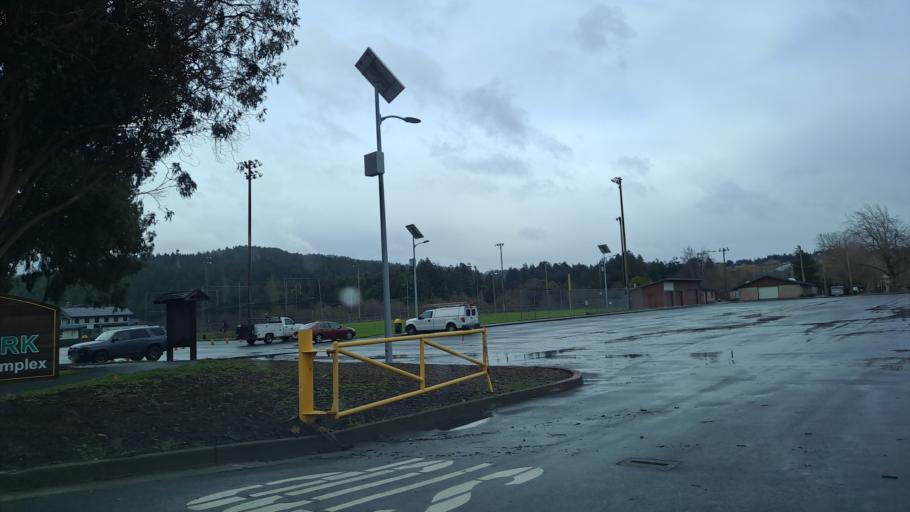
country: US
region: California
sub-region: Humboldt County
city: Fortuna
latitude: 40.5933
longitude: -124.1372
